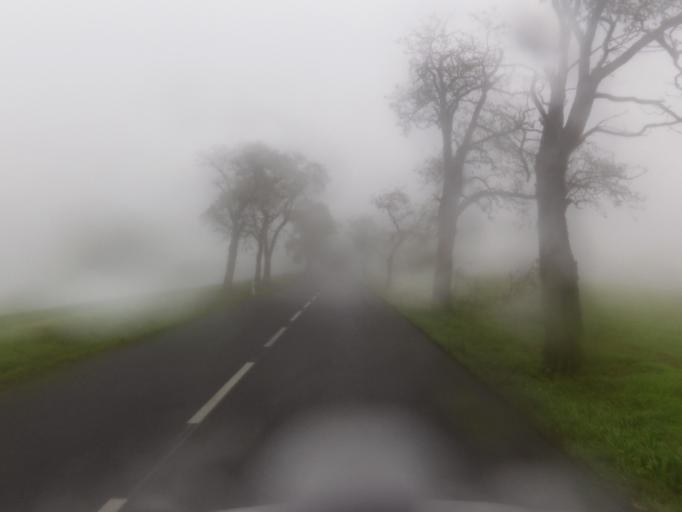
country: CZ
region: Ustecky
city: Postoloprty
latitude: 50.3179
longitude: 13.7178
